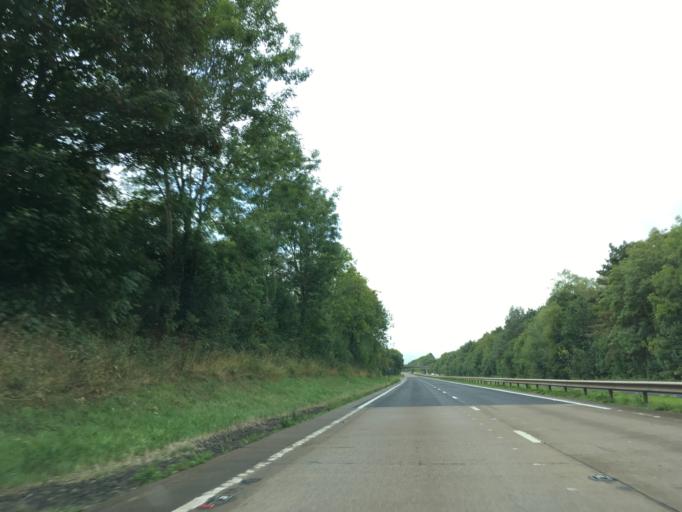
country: GB
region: Wales
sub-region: Monmouthshire
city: Llanarth
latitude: 51.7816
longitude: -2.9177
